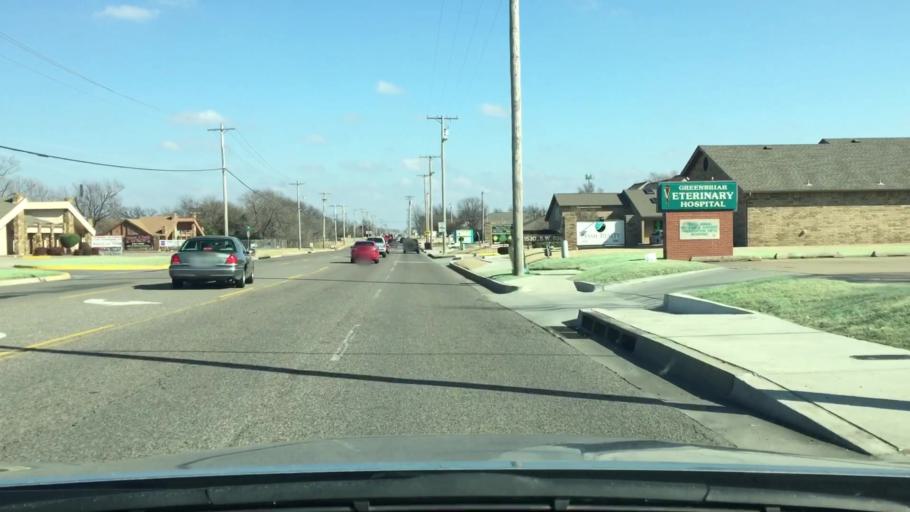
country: US
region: Oklahoma
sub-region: Cleveland County
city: Moore
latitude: 35.3771
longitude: -97.5456
